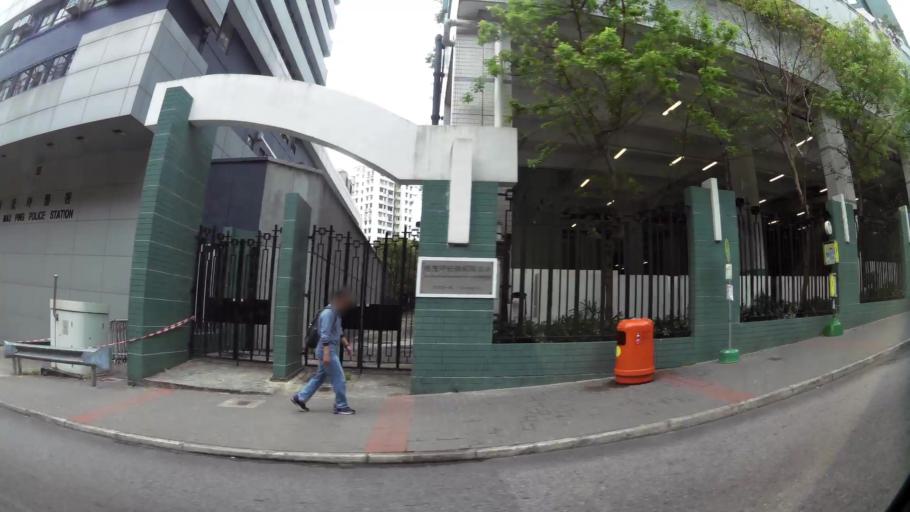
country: HK
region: Kowloon City
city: Kowloon
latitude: 22.3215
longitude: 114.2244
